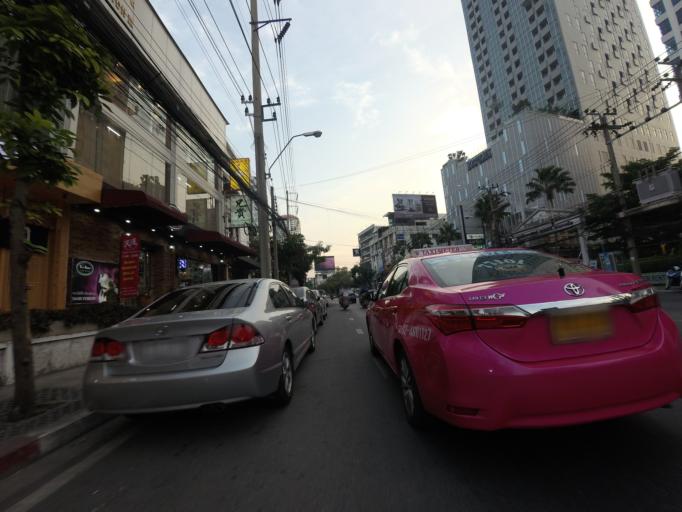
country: TH
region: Bangkok
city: Watthana
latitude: 13.7295
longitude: 100.5812
